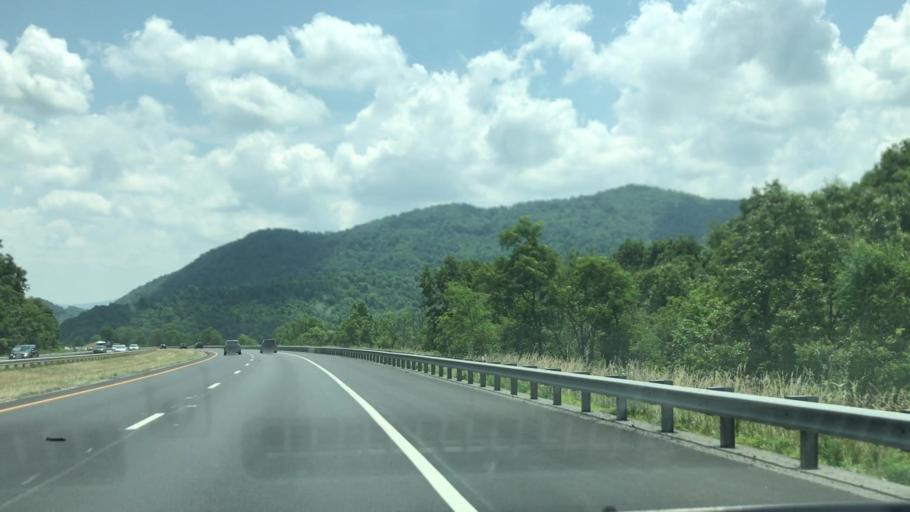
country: US
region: Virginia
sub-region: Wythe County
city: Wytheville
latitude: 37.0062
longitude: -81.0996
